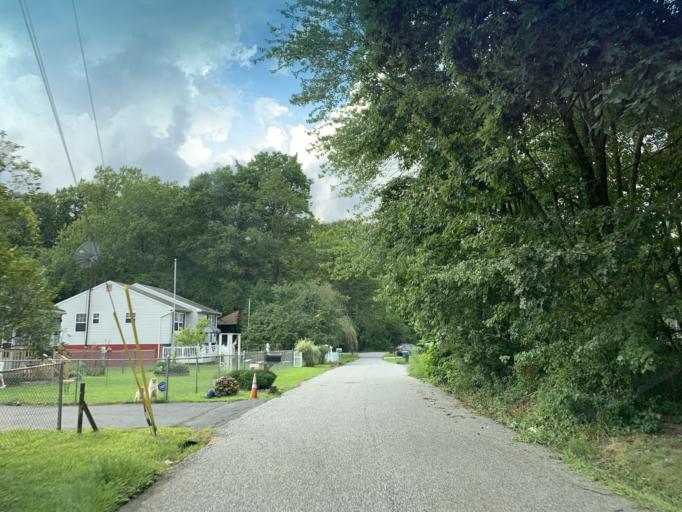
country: US
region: Maryland
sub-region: Baltimore County
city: Essex
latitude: 39.2912
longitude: -76.4428
